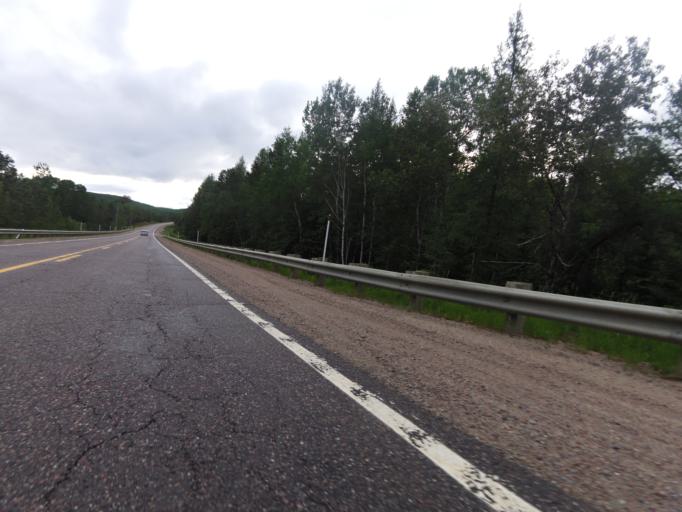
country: CA
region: Quebec
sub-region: Outaouais
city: Shawville
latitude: 45.9070
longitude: -76.2961
